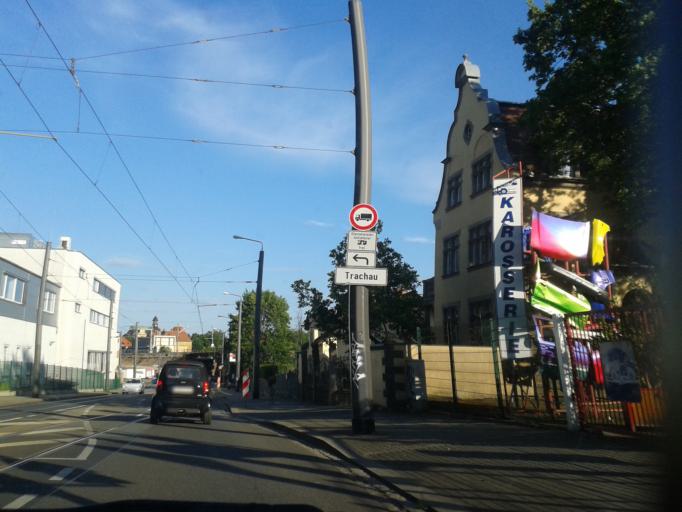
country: DE
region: Saxony
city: Radebeul
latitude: 51.0915
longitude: 13.7010
